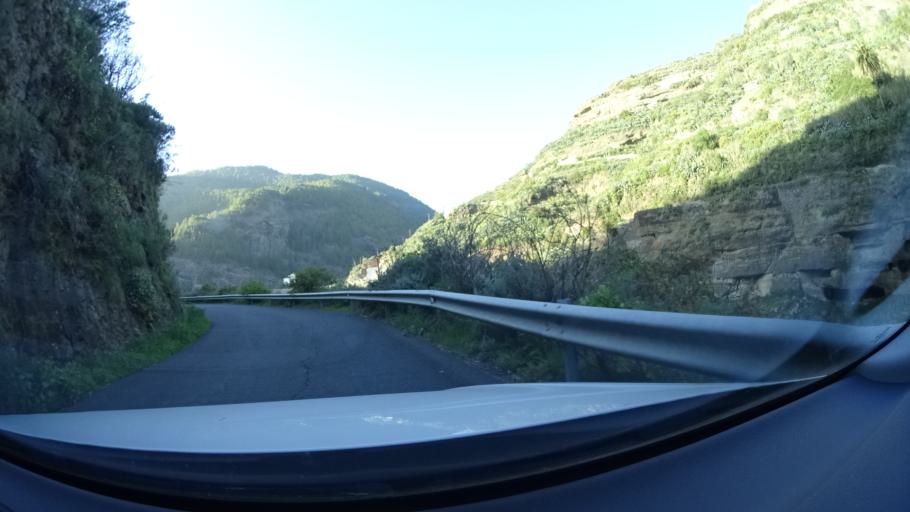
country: ES
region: Canary Islands
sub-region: Provincia de Las Palmas
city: Artenara
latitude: 28.0475
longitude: -15.6671
